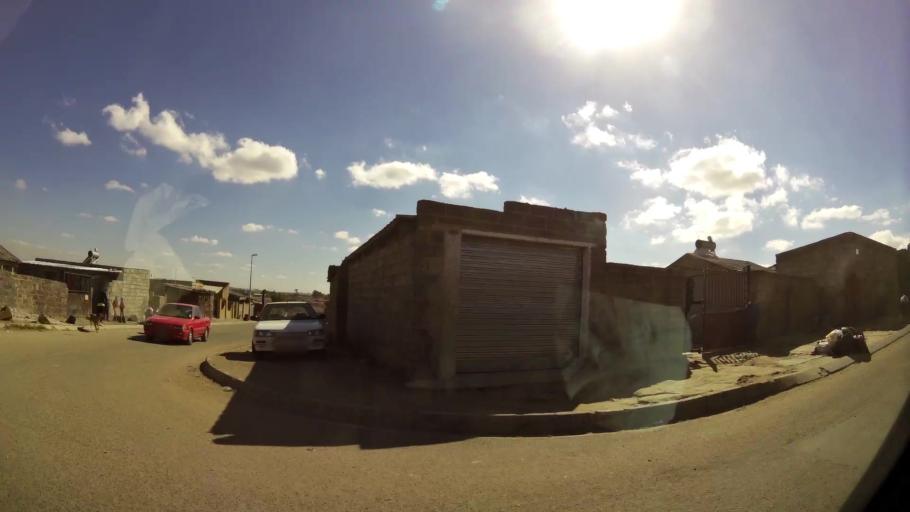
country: ZA
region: Gauteng
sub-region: City of Johannesburg Metropolitan Municipality
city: Midrand
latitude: -26.0327
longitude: 28.1642
